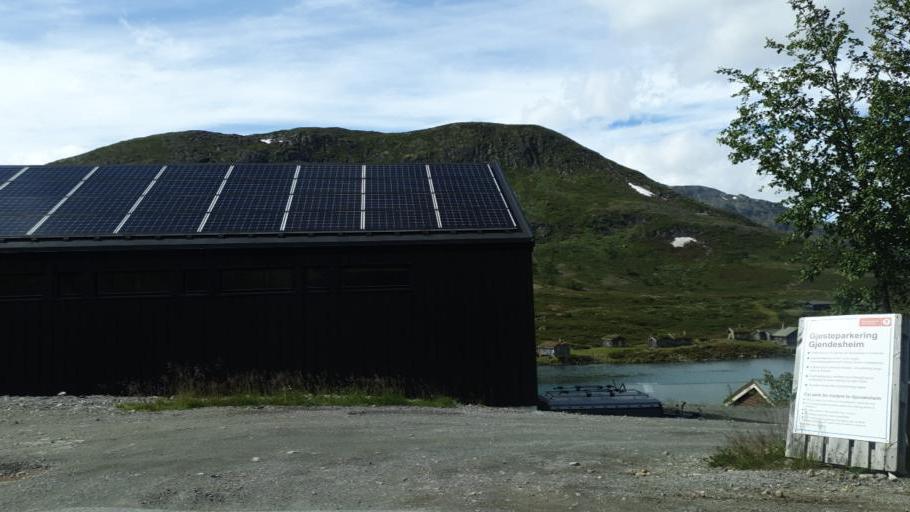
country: NO
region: Oppland
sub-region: Lom
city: Fossbergom
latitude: 61.4937
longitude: 8.8146
